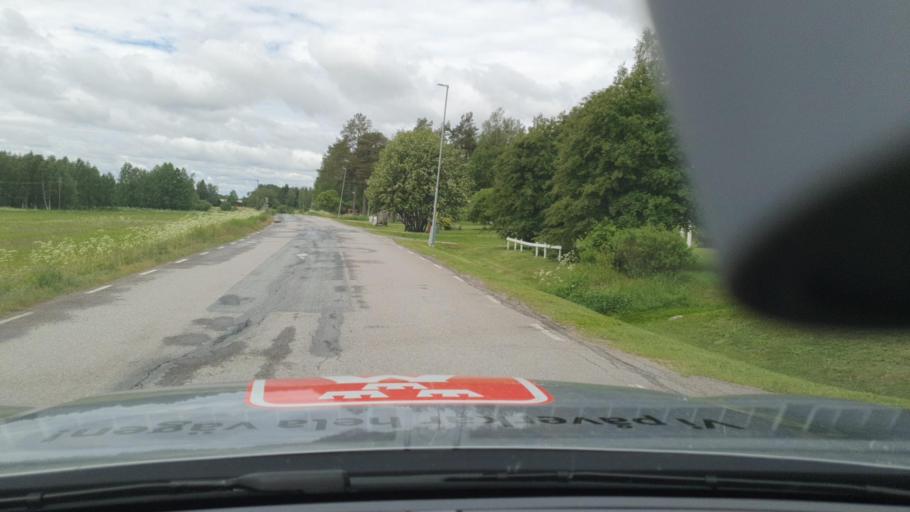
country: SE
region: Norrbotten
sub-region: Lulea Kommun
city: Ranea
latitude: 65.7738
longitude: 22.2455
